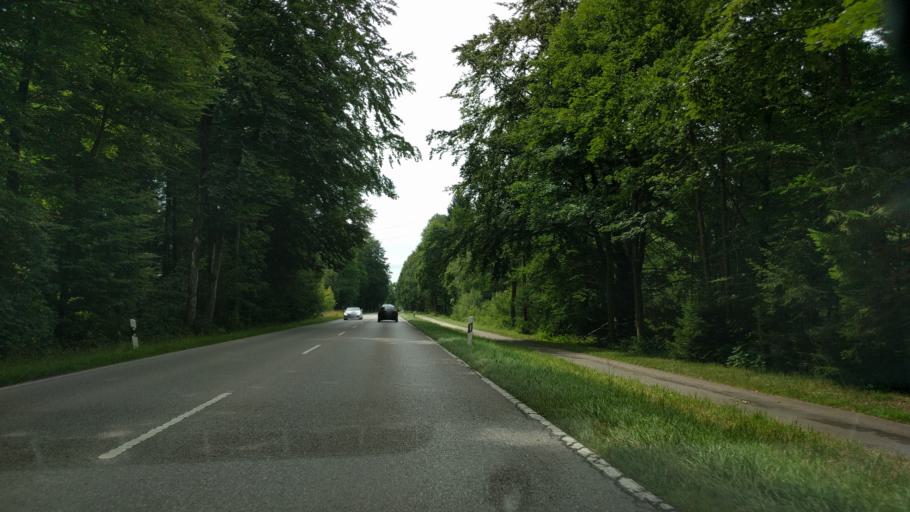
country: DE
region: Bavaria
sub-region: Upper Bavaria
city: Strasslach-Dingharting
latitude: 48.0181
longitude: 11.5170
